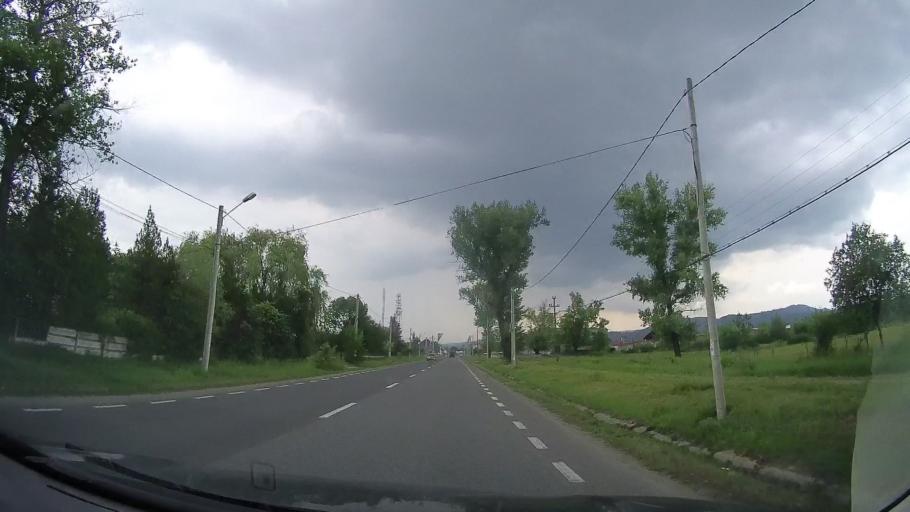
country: RO
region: Caras-Severin
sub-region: Municipiul Caransebes
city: Caransebes
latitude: 45.4318
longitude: 22.1951
